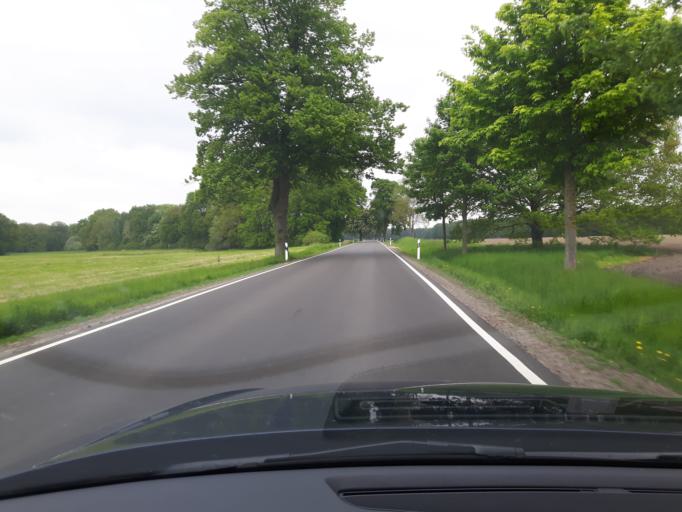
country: DE
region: Mecklenburg-Vorpommern
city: Gnoien
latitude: 53.9913
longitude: 12.6845
